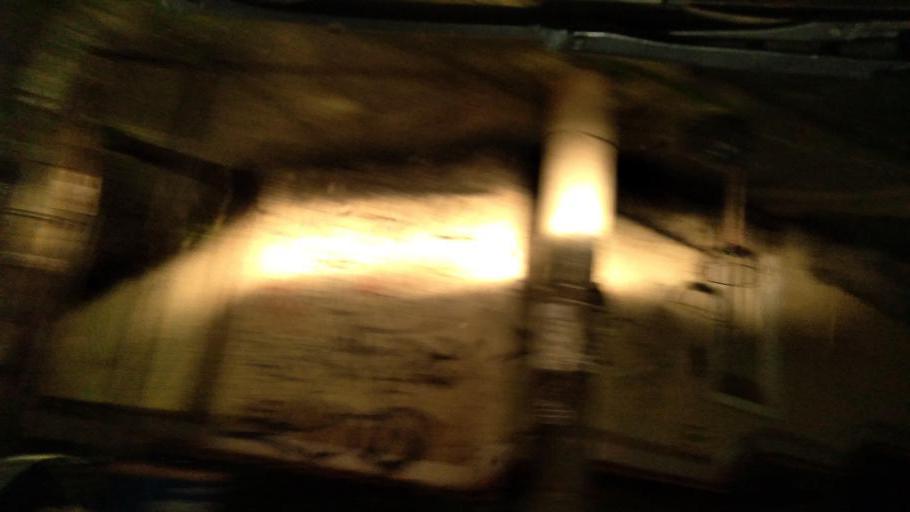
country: BR
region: Minas Gerais
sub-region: Belo Horizonte
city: Belo Horizonte
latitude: -19.9006
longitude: -43.9191
